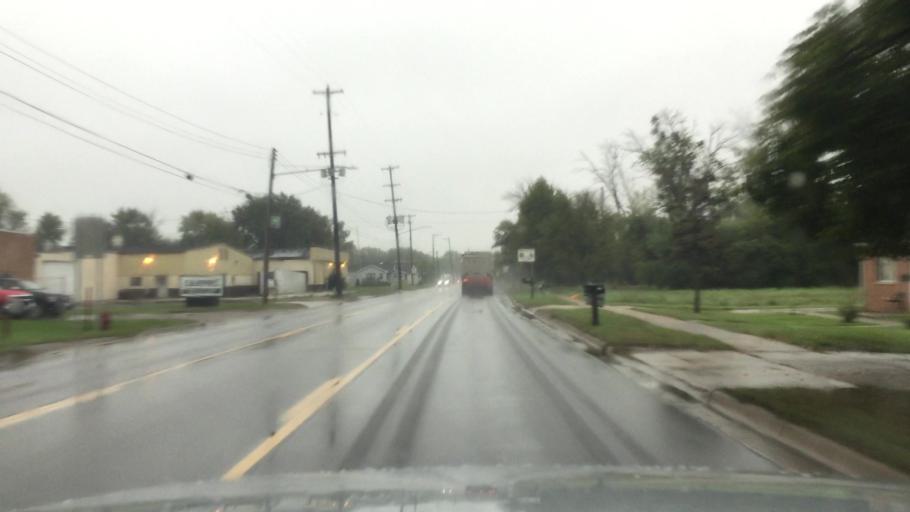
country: US
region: Michigan
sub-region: Saginaw County
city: Saginaw
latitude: 43.3930
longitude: -83.9556
